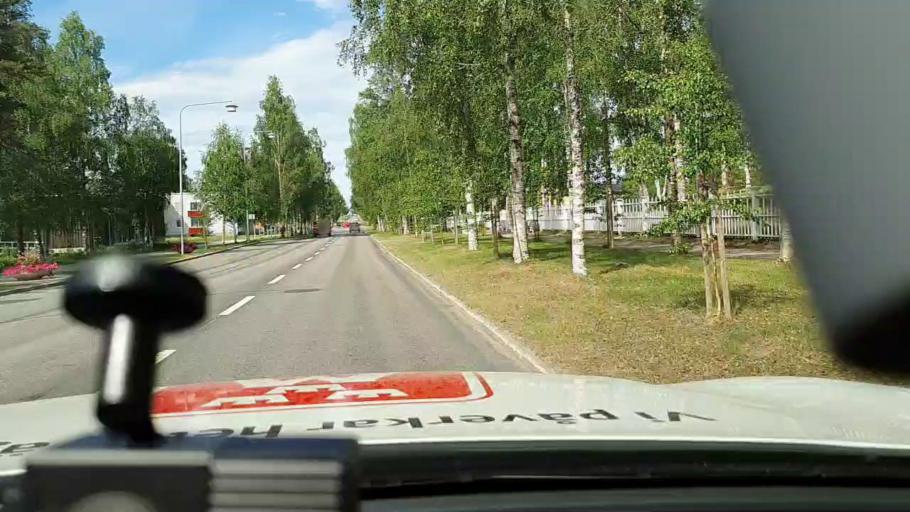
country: SE
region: Norrbotten
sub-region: Jokkmokks Kommun
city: Jokkmokk
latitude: 66.6044
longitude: 19.8426
